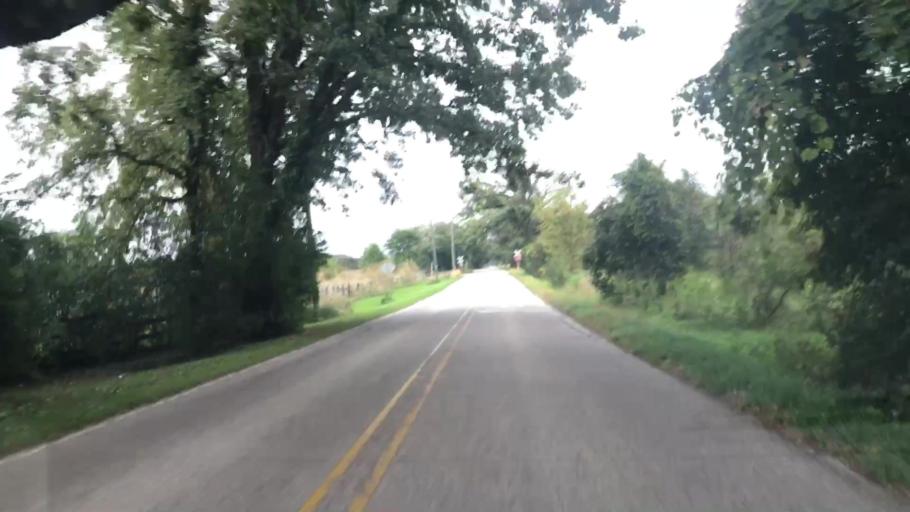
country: US
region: Wisconsin
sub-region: Waukesha County
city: North Prairie
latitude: 42.9152
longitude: -88.4367
